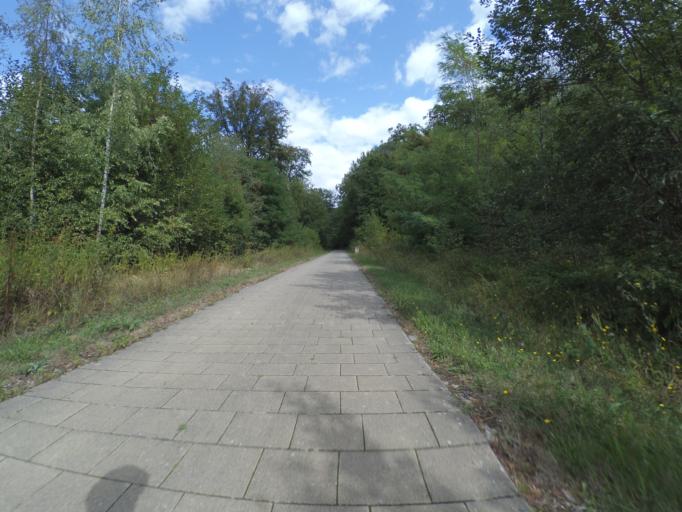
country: LU
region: Grevenmacher
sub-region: Canton de Remich
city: Bous
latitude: 49.5237
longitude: 6.3175
